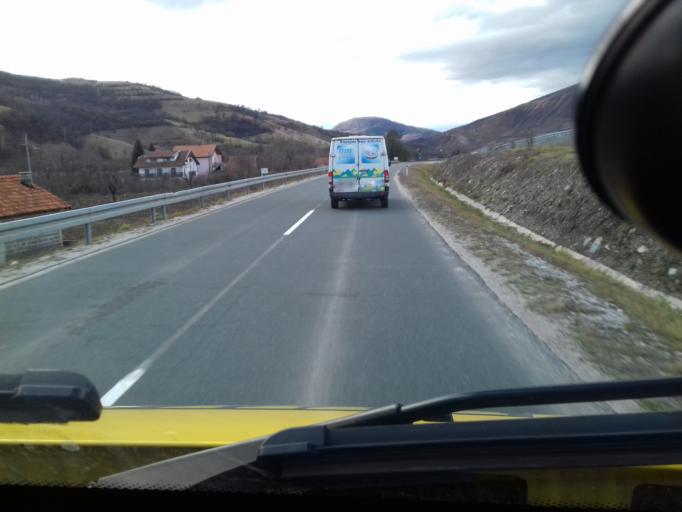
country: BA
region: Federation of Bosnia and Herzegovina
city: Kacuni
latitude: 44.1333
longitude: 18.0162
